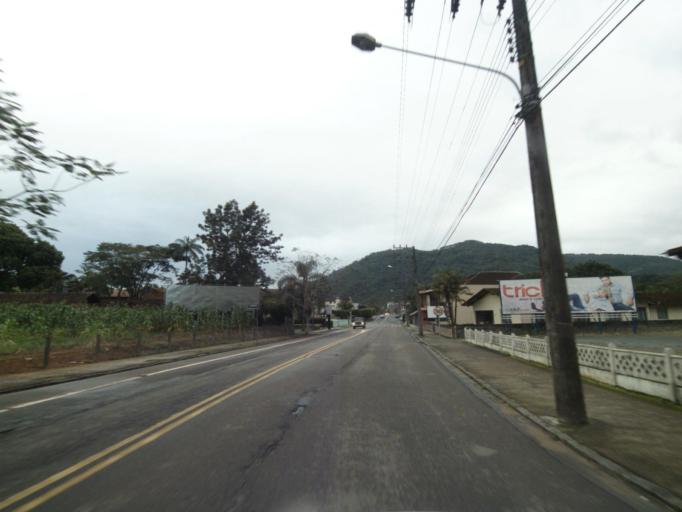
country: BR
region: Santa Catarina
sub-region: Pomerode
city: Pomerode
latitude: -26.7271
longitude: -49.1736
